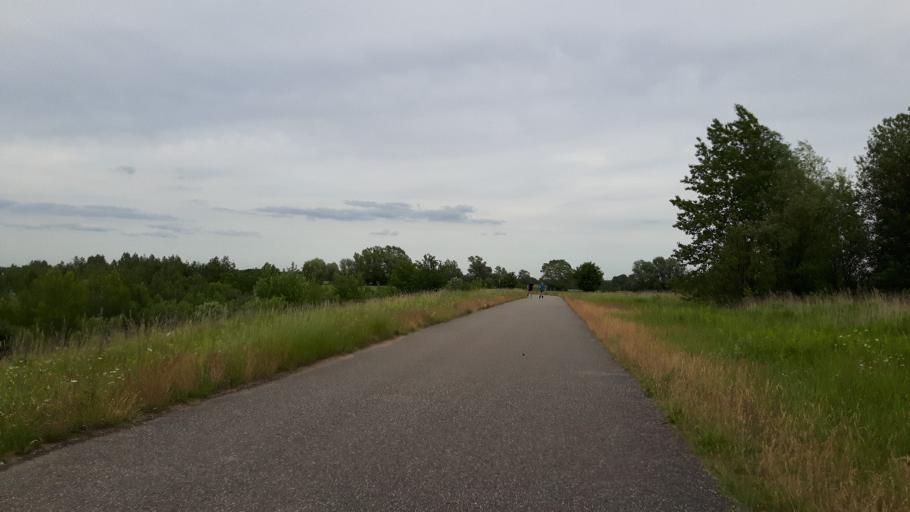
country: DE
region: Saxony
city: Rackwitz
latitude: 51.4296
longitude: 12.3332
